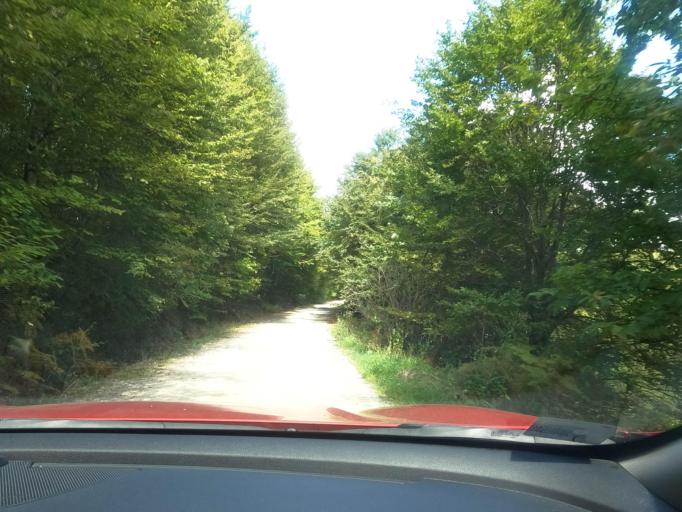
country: BA
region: Federation of Bosnia and Herzegovina
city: Velika Kladusa
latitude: 45.2743
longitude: 15.7789
